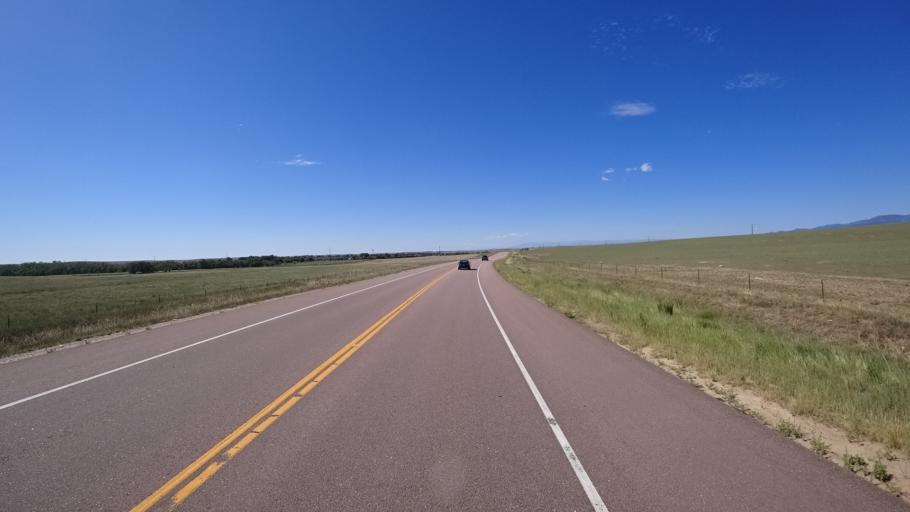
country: US
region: Colorado
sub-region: El Paso County
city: Security-Widefield
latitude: 38.7915
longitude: -104.6573
